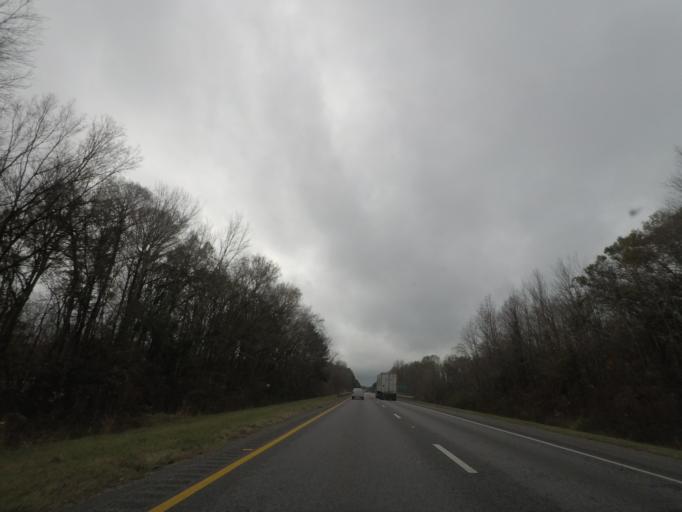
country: US
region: South Carolina
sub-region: Orangeburg County
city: Holly Hill
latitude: 33.3406
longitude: -80.5356
